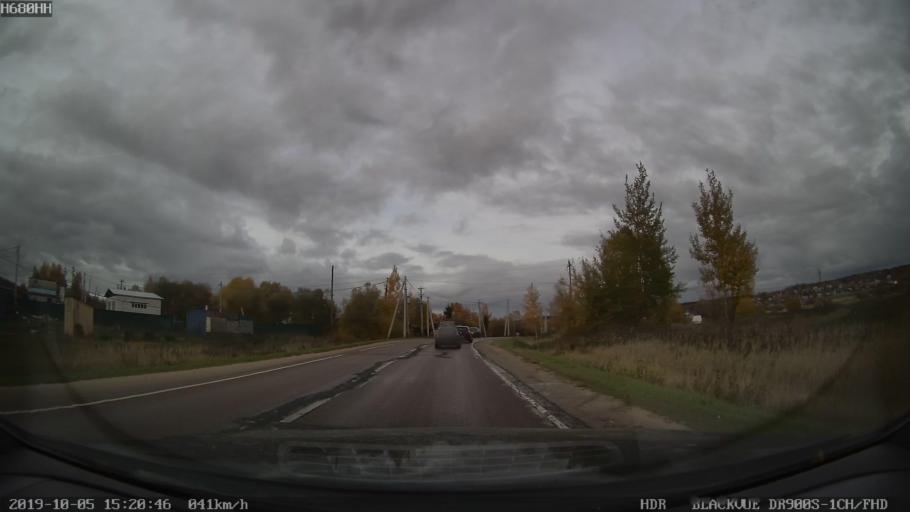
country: RU
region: Moskovskaya
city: Solnechnogorsk
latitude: 56.2250
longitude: 36.9073
